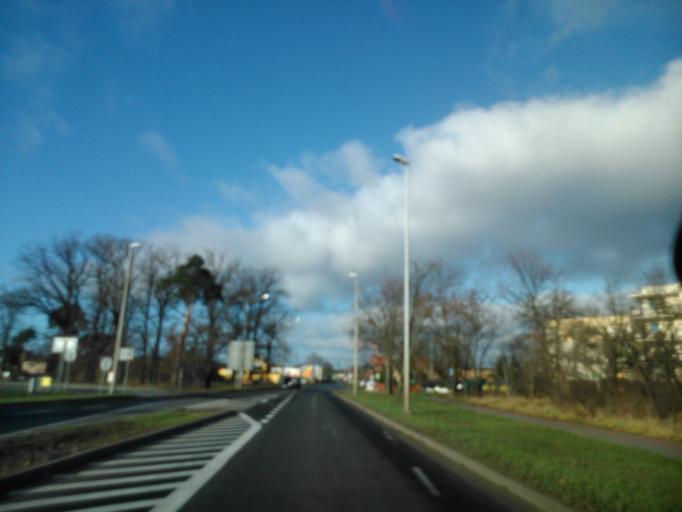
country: PL
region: Kujawsko-Pomorskie
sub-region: Torun
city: Torun
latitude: 52.9928
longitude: 18.6313
